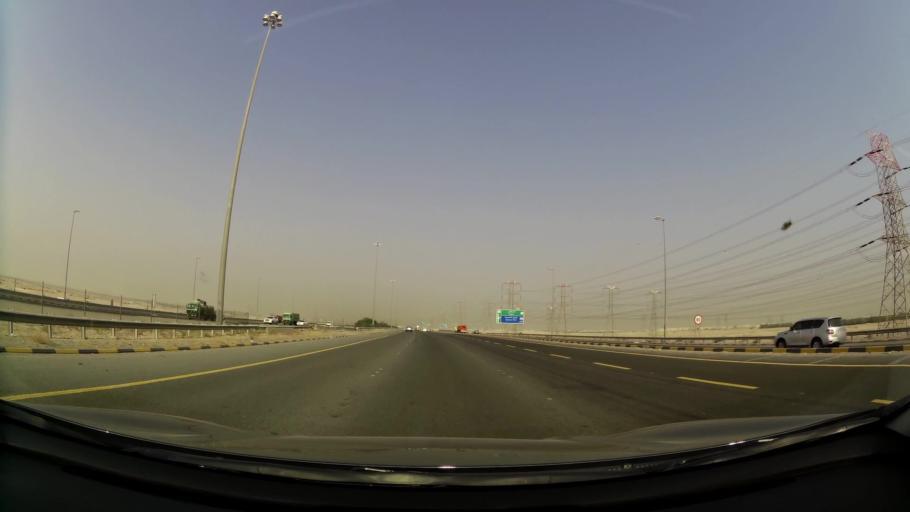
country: KW
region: Al Asimah
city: Ar Rabiyah
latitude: 29.2463
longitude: 47.8745
